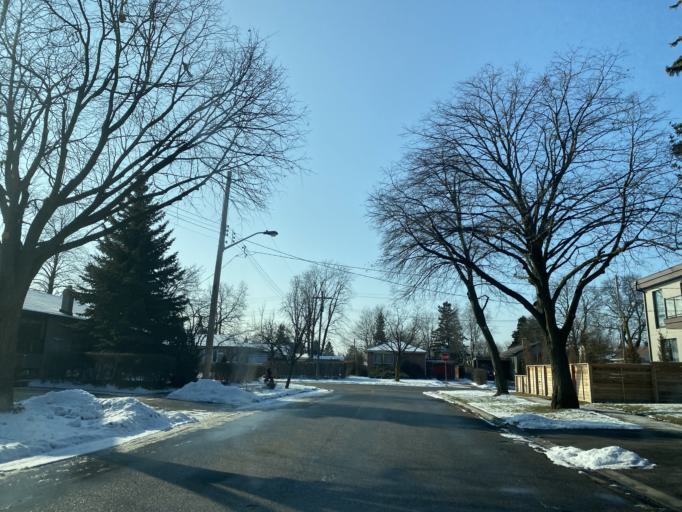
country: CA
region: Ontario
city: Etobicoke
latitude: 43.6655
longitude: -79.5616
